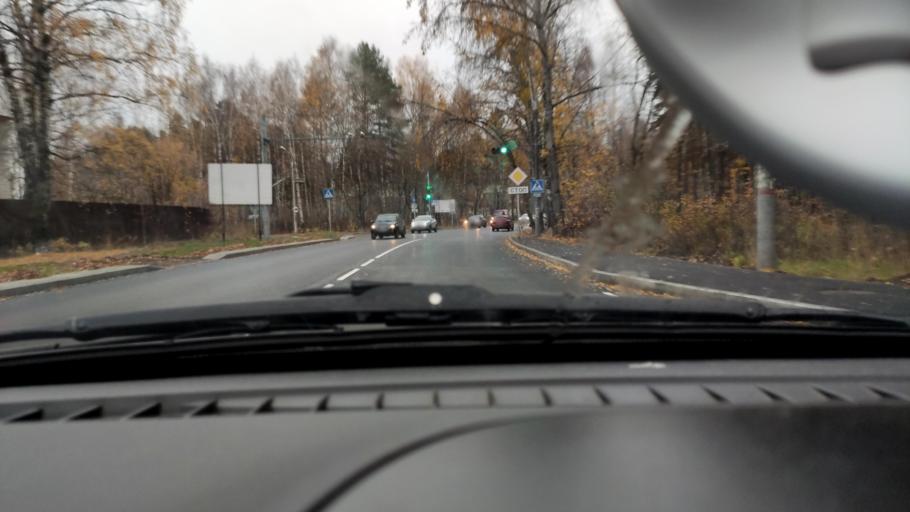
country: RU
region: Perm
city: Kondratovo
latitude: 58.0217
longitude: 56.0124
